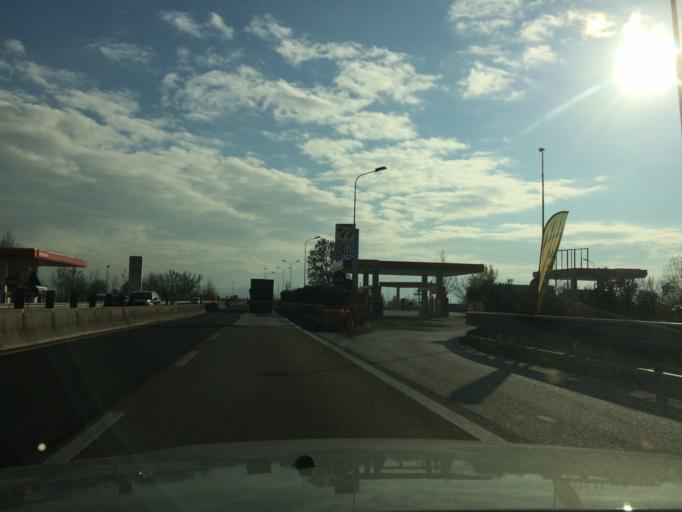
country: IT
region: Umbria
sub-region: Provincia di Terni
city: San Gemini
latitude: 42.5768
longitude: 12.5738
